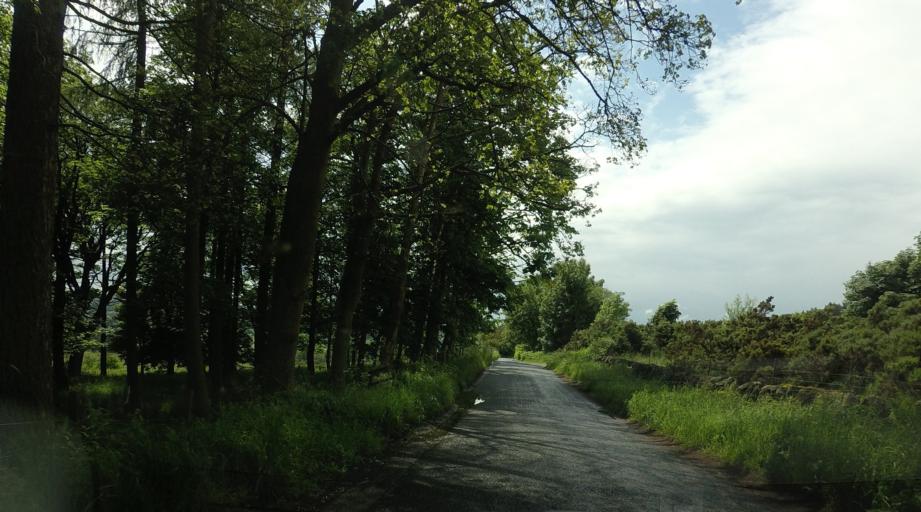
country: GB
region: Scotland
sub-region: Fife
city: Kelty
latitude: 56.1550
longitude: -3.3667
